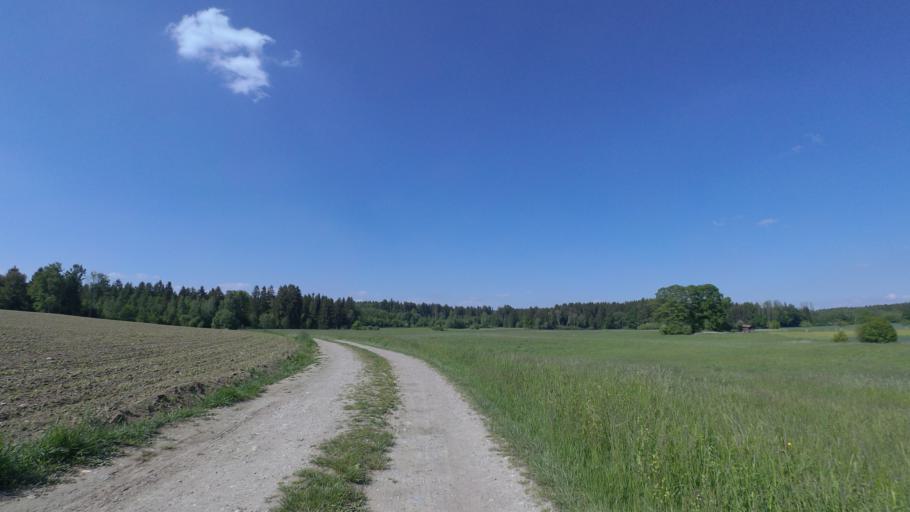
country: DE
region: Bavaria
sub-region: Upper Bavaria
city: Chieming
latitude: 47.9109
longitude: 12.5087
